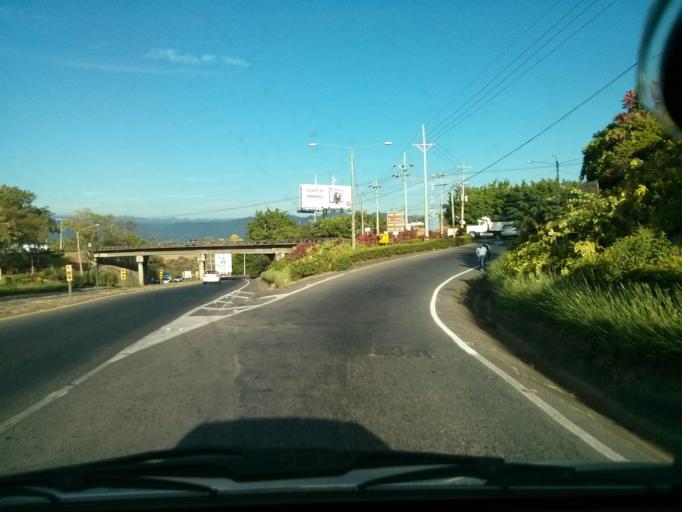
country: CR
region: Alajuela
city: Carrillos
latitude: 10.0044
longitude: -84.2912
